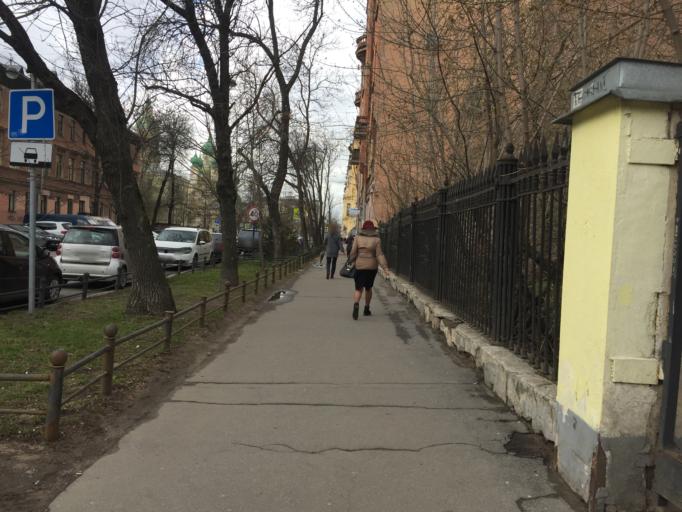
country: RU
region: St.-Petersburg
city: Vasyl'evsky Ostrov
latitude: 59.9442
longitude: 30.2774
